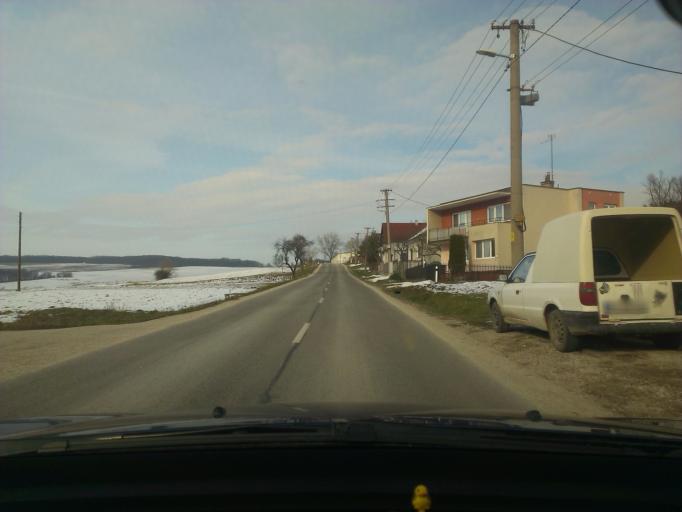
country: SK
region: Nitriansky
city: Stara Tura
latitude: 48.7084
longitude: 17.6845
